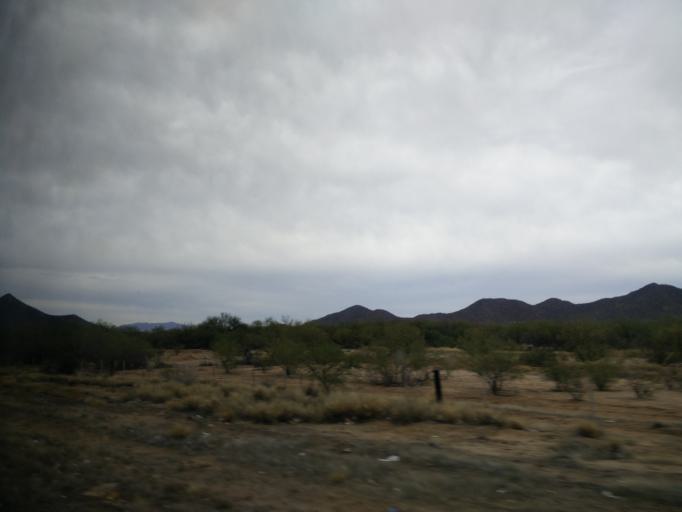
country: MX
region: Sonora
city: Hermosillo
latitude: 28.7907
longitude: -110.9613
